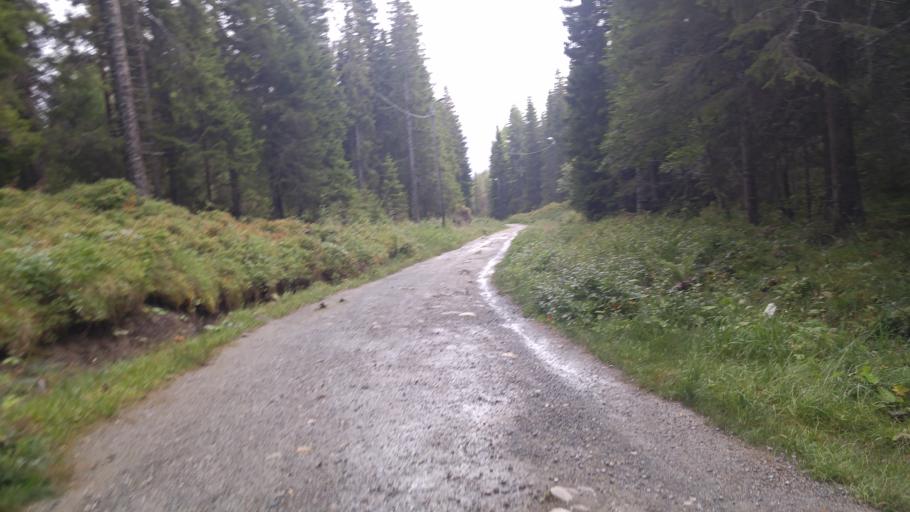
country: NO
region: Sor-Trondelag
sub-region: Trondheim
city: Trondheim
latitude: 63.4115
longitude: 10.3315
